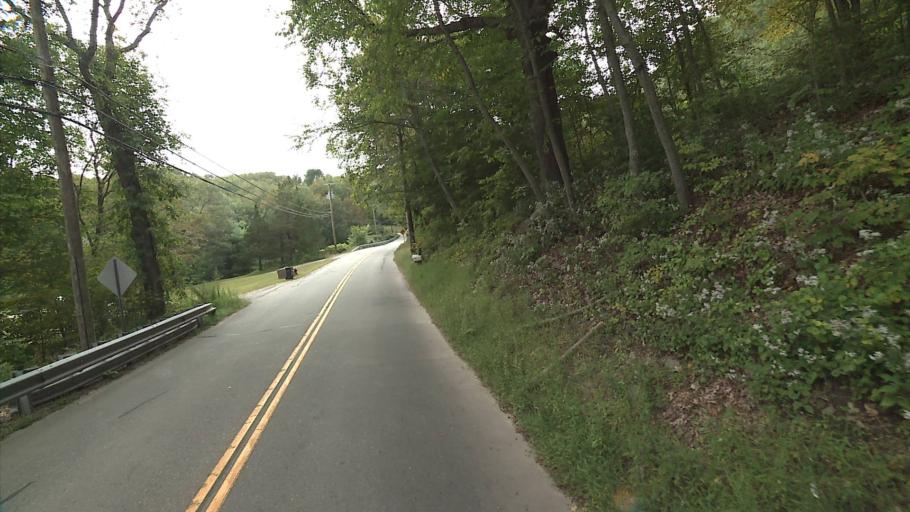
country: US
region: Connecticut
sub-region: Tolland County
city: South Coventry
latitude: 41.7805
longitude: -72.2840
